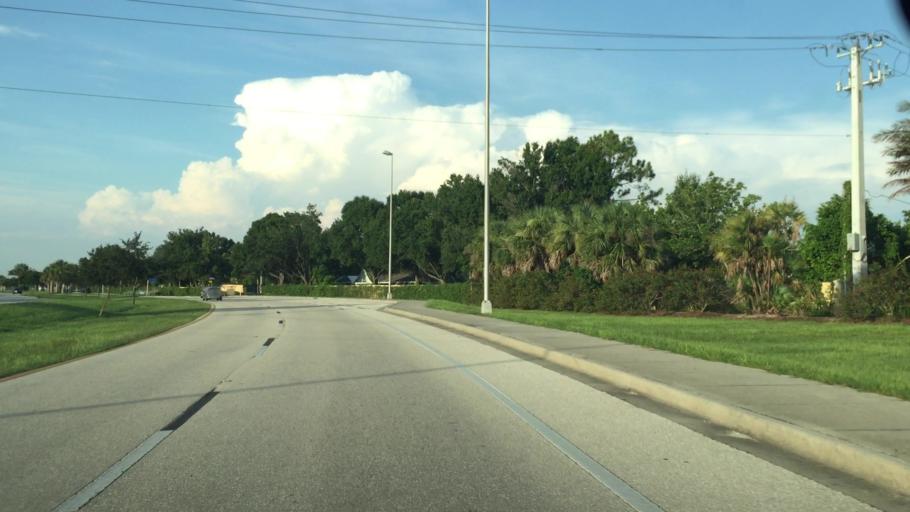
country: US
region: Florida
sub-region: Lee County
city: Three Oaks
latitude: 26.4567
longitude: -81.7886
